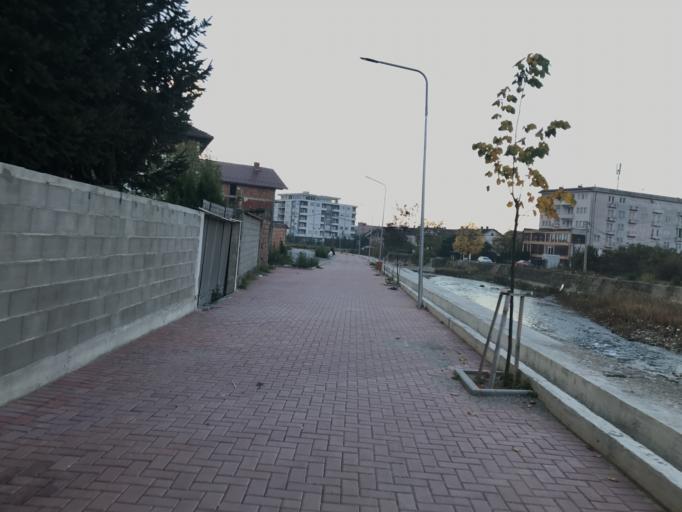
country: XK
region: Pec
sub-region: Komuna e Pejes
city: Peje
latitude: 42.6563
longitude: 20.2966
